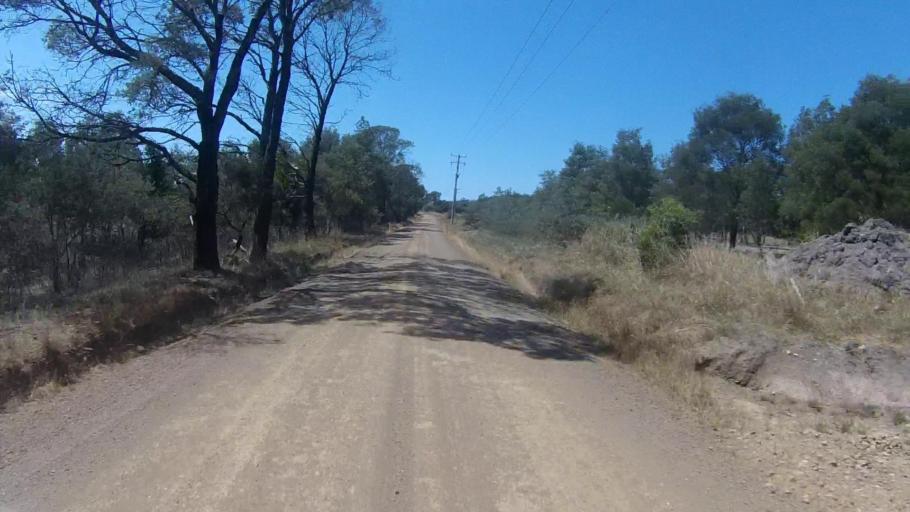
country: AU
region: Tasmania
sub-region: Sorell
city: Sorell
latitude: -42.8266
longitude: 147.6463
